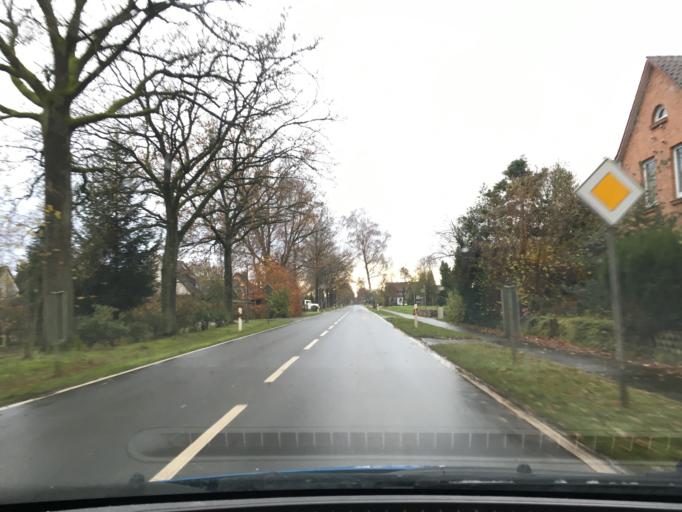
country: DE
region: Lower Saxony
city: Wriedel
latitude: 53.0020
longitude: 10.2618
